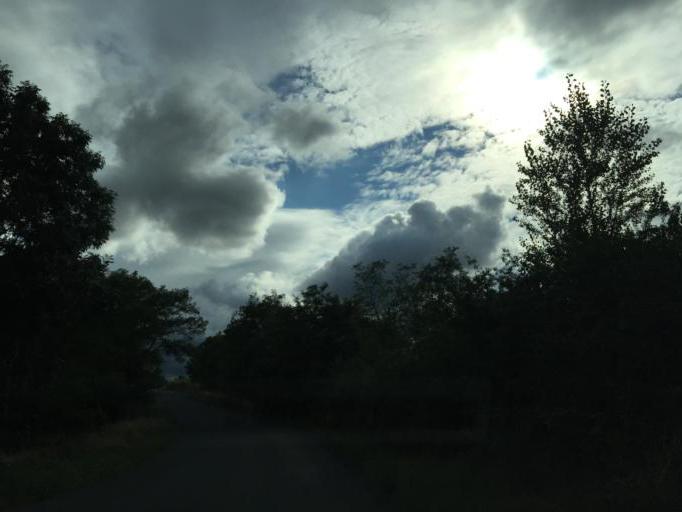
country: FR
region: Rhone-Alpes
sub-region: Departement de la Loire
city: La Grand-Croix
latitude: 45.5055
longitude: 4.5388
